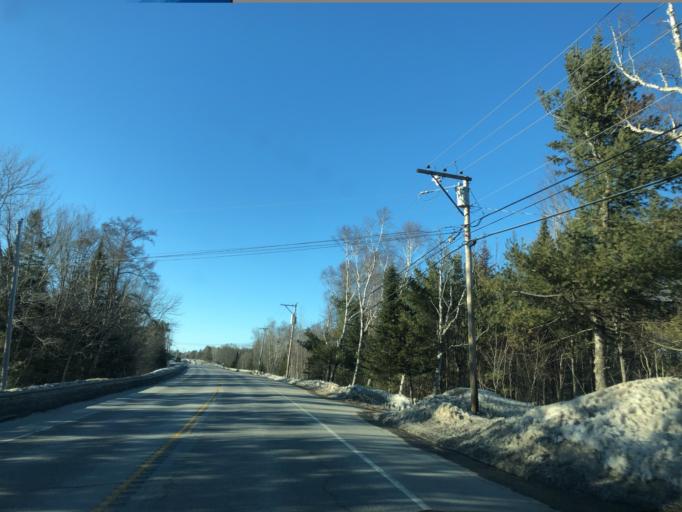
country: US
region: Maine
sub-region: Penobscot County
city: Kenduskeag
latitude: 44.9476
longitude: -68.9458
